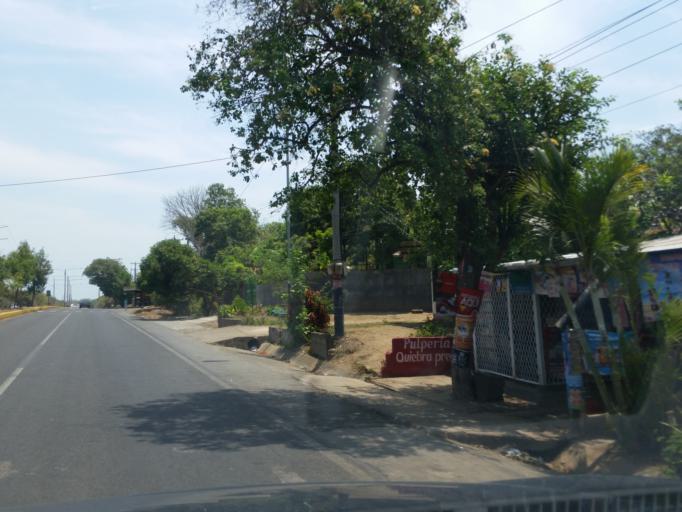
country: NI
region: Granada
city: Granada
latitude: 11.9682
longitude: -86.0150
